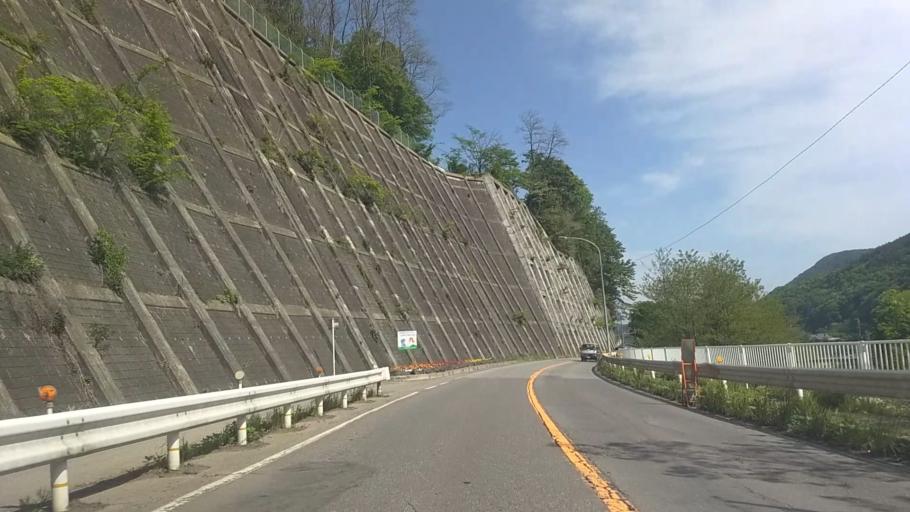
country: JP
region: Nagano
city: Saku
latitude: 36.1062
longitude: 138.4793
